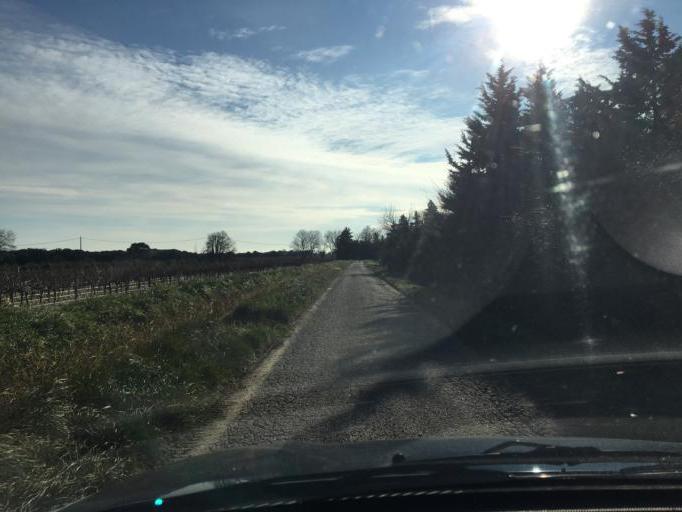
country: FR
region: Provence-Alpes-Cote d'Azur
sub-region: Departement du Vaucluse
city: Camaret-sur-Aigues
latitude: 44.1559
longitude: 4.8909
